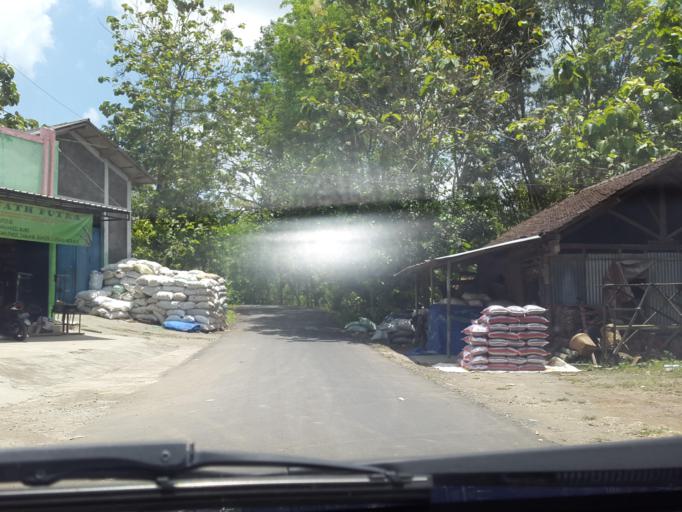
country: ID
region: Daerah Istimewa Yogyakarta
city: Wonosari
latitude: -7.9234
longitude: 110.7408
